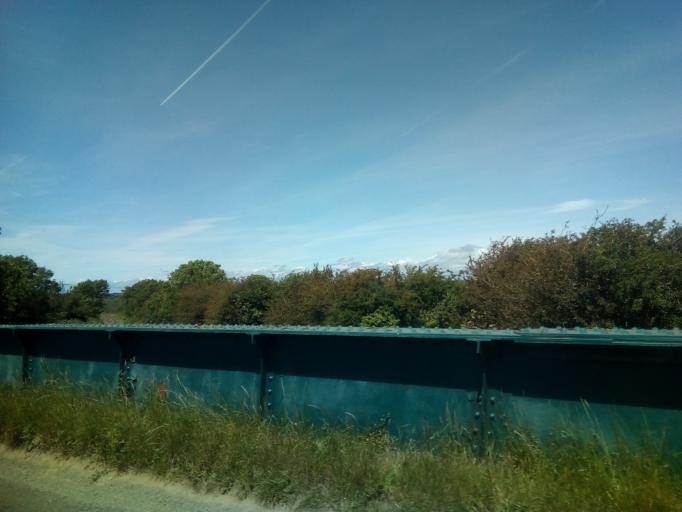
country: IE
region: Leinster
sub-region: Loch Garman
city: Loch Garman
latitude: 52.2350
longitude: -6.5896
